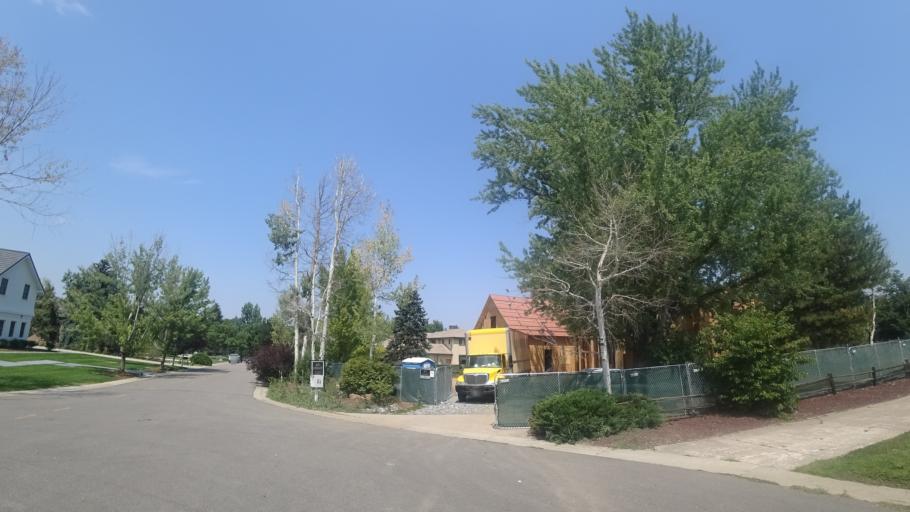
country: US
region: Colorado
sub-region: Arapahoe County
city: Greenwood Village
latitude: 39.6213
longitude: -104.9725
